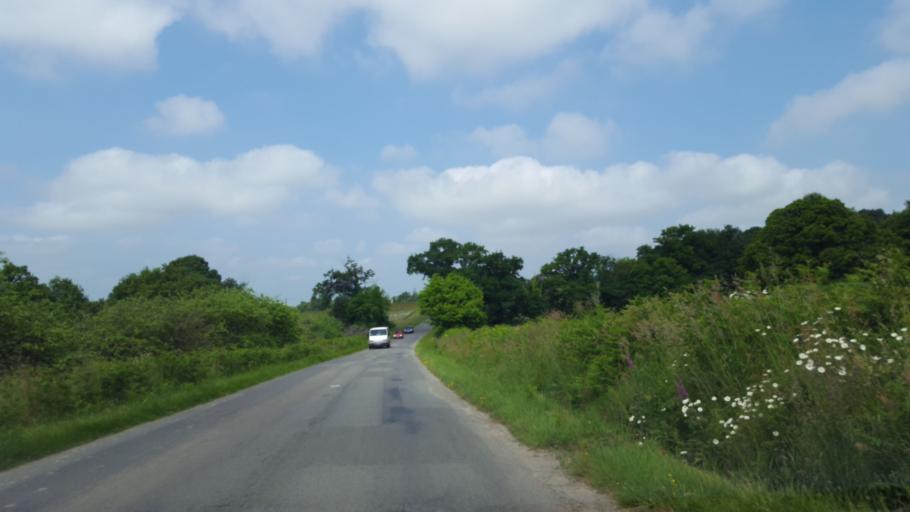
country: FR
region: Brittany
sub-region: Departement d'Ille-et-Vilaine
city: Baulon
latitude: 47.9268
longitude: -1.9267
